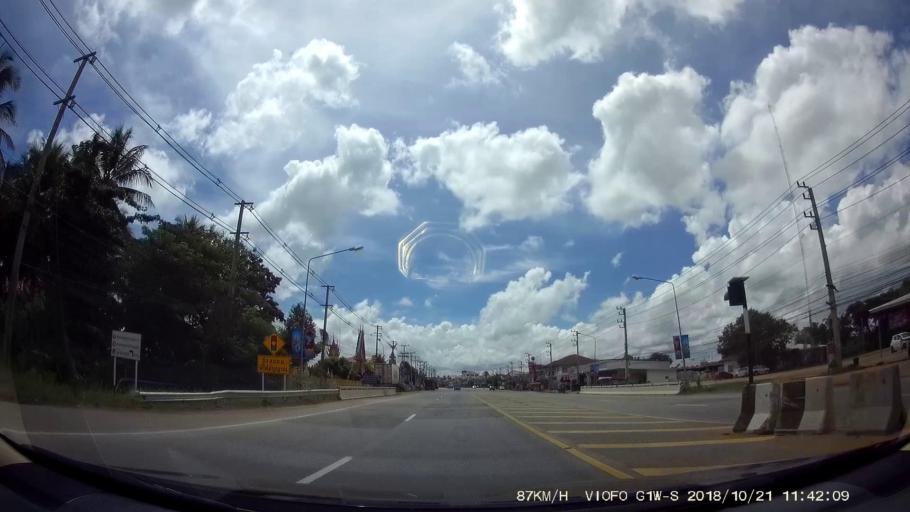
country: TH
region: Chaiyaphum
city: Chaiyaphum
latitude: 15.6896
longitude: 102.0113
